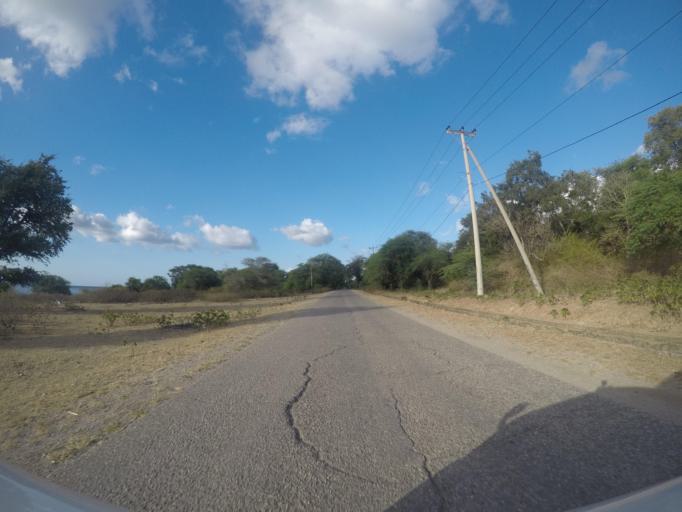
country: TL
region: Lautem
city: Lospalos
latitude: -8.3584
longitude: 126.9086
